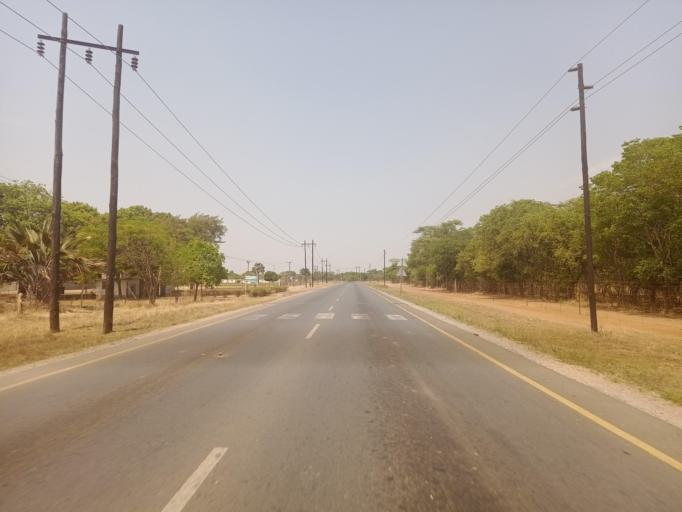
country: ZM
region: Lusaka
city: Lusaka
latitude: -15.2806
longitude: 28.3932
